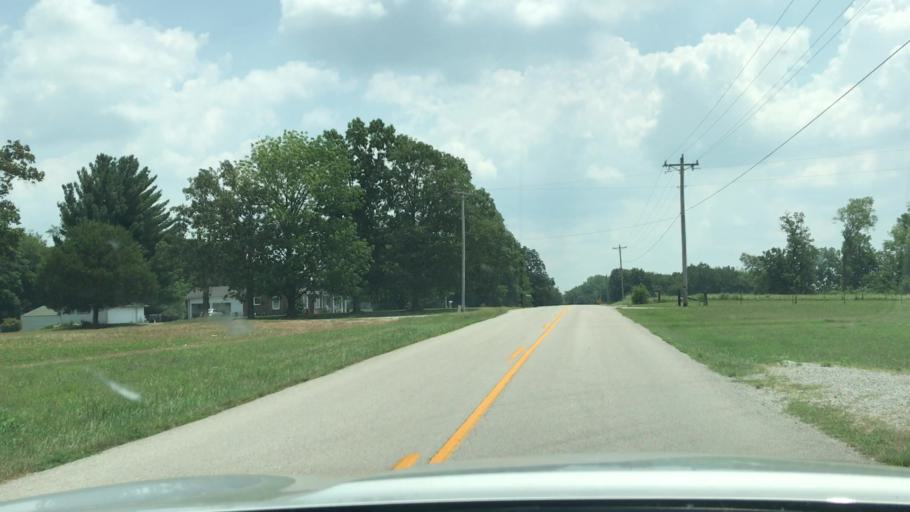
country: US
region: Kentucky
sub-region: Todd County
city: Elkton
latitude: 36.7641
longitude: -87.1077
